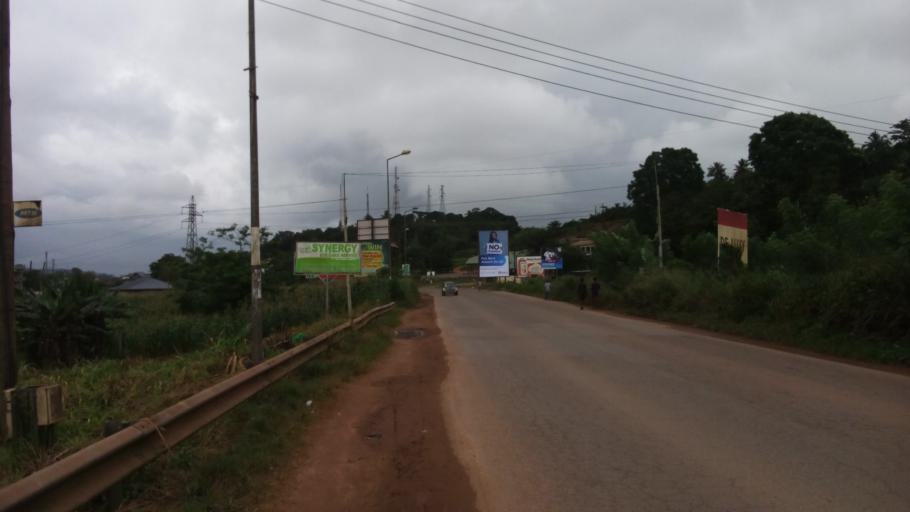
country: GH
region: Western
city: Tarkwa
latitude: 5.2990
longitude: -1.9988
